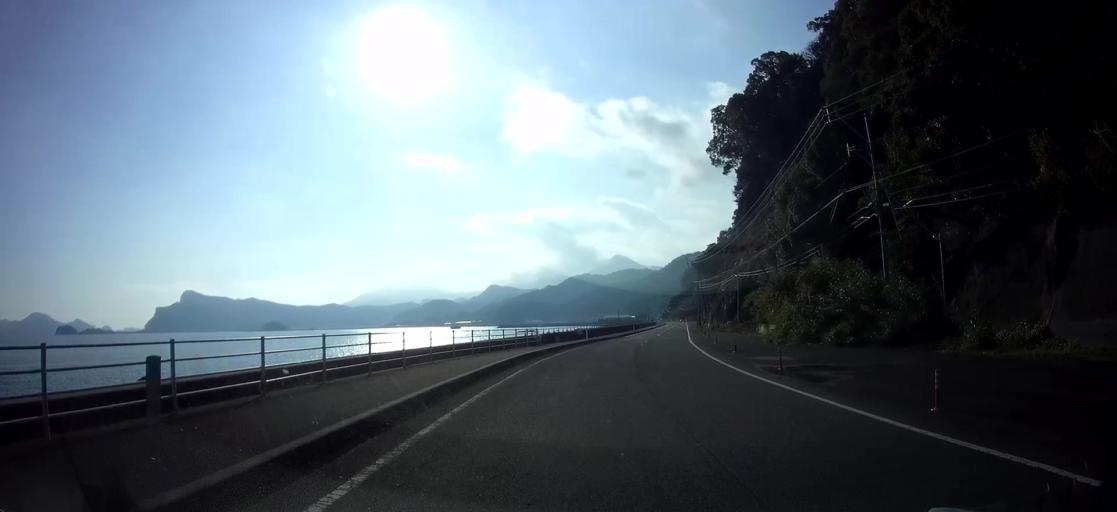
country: JP
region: Kumamoto
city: Yatsushiro
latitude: 32.4546
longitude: 130.4275
